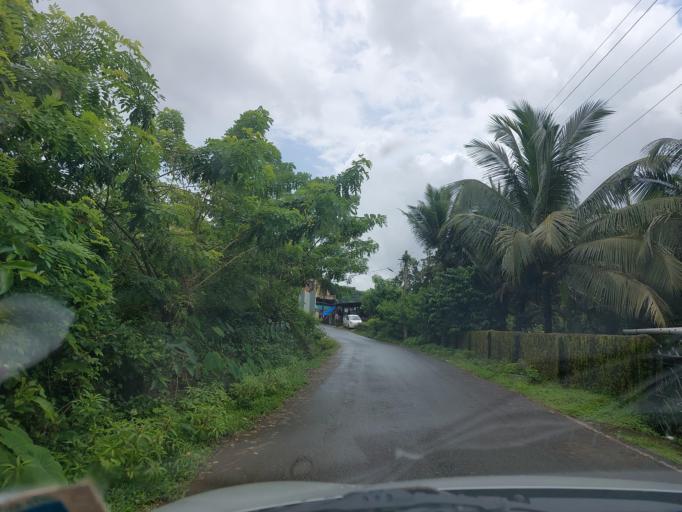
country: IN
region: Goa
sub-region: North Goa
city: Valpoy
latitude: 15.5386
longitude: 74.1400
